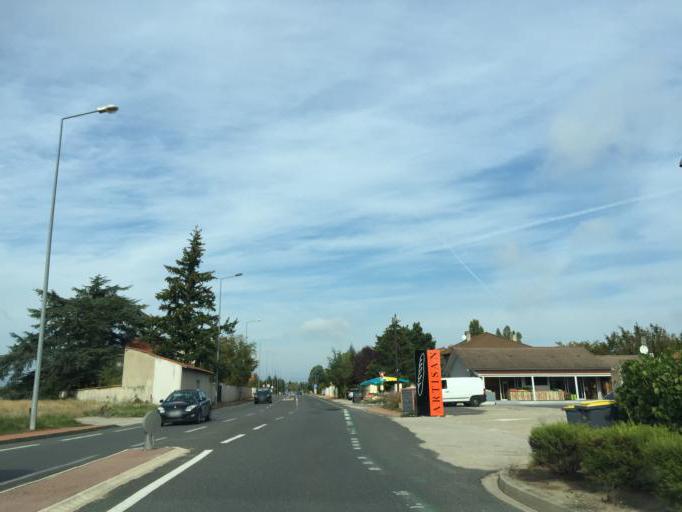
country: FR
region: Rhone-Alpes
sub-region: Departement de la Loire
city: Bonson
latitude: 45.5255
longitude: 4.2102
